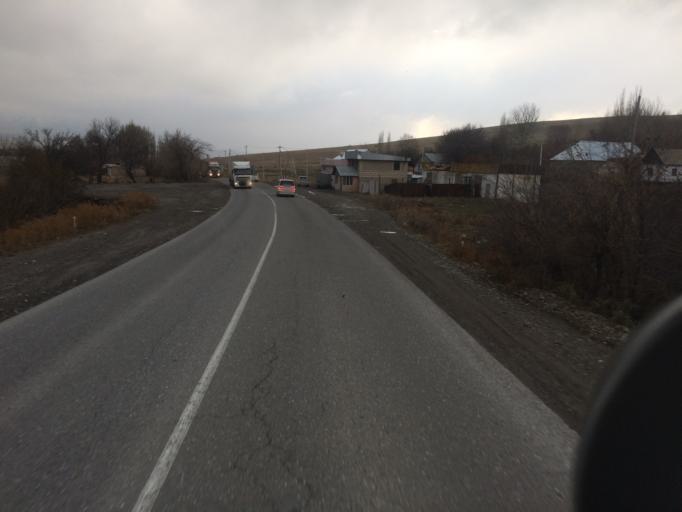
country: KZ
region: Ongtustik Qazaqstan
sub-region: Tulkibas Audany
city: Zhabagly
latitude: 42.5179
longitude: 70.5844
